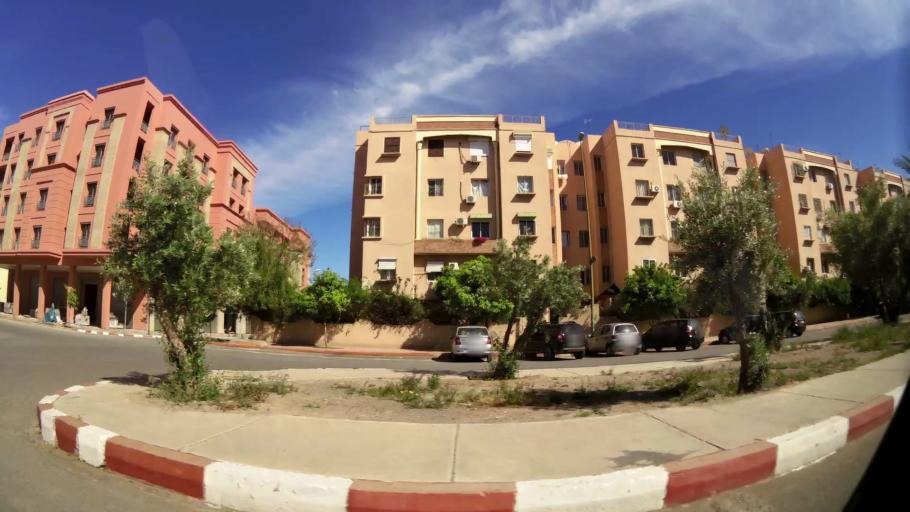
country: MA
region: Marrakech-Tensift-Al Haouz
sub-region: Marrakech
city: Marrakesh
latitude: 31.6671
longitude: -8.0310
